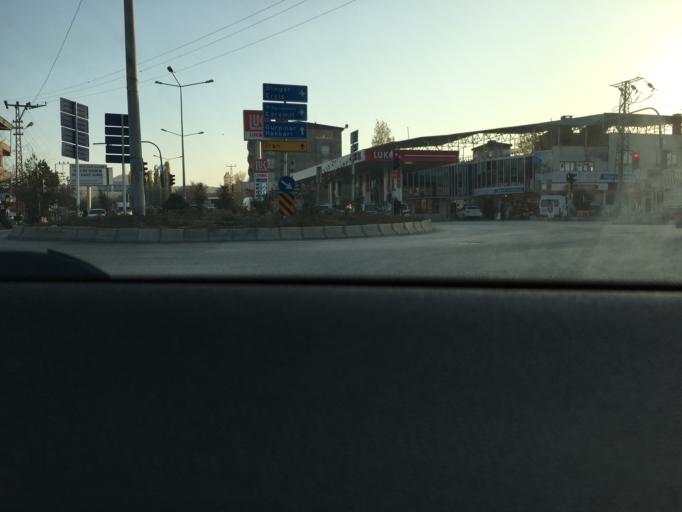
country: TR
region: Van
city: Van
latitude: 38.4790
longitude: 43.3902
